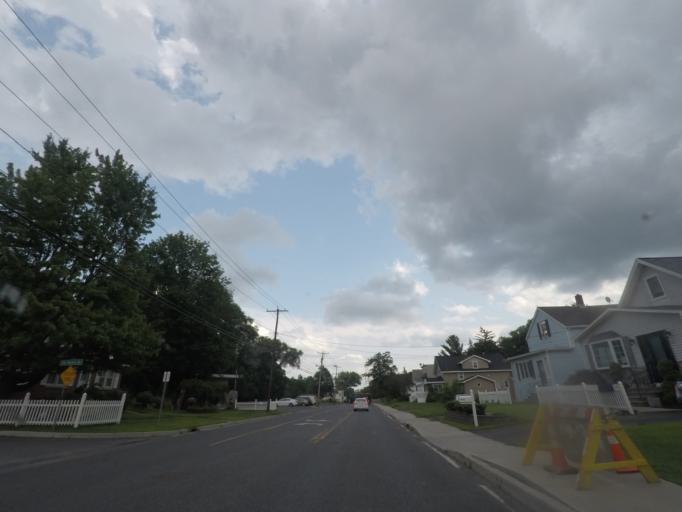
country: US
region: New York
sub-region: Albany County
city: West Albany
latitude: 42.6903
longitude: -73.7835
